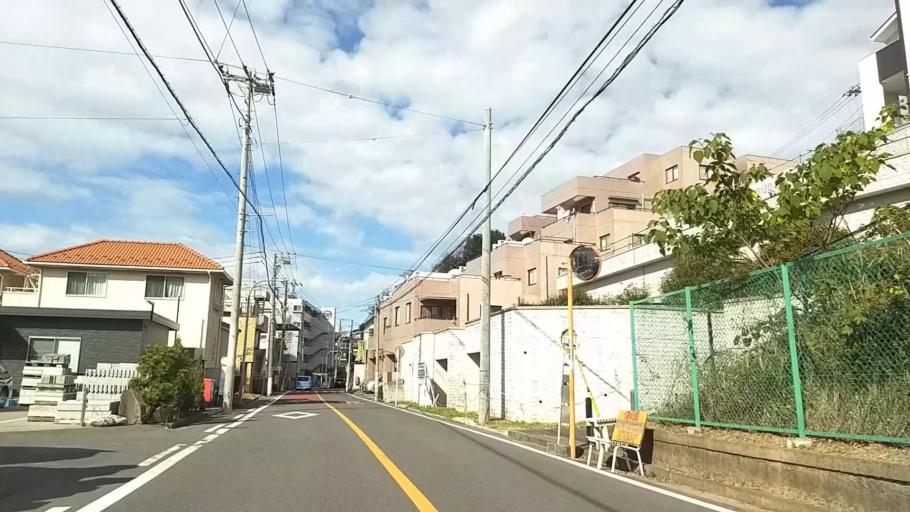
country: JP
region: Kanagawa
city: Yokohama
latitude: 35.5035
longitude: 139.6605
